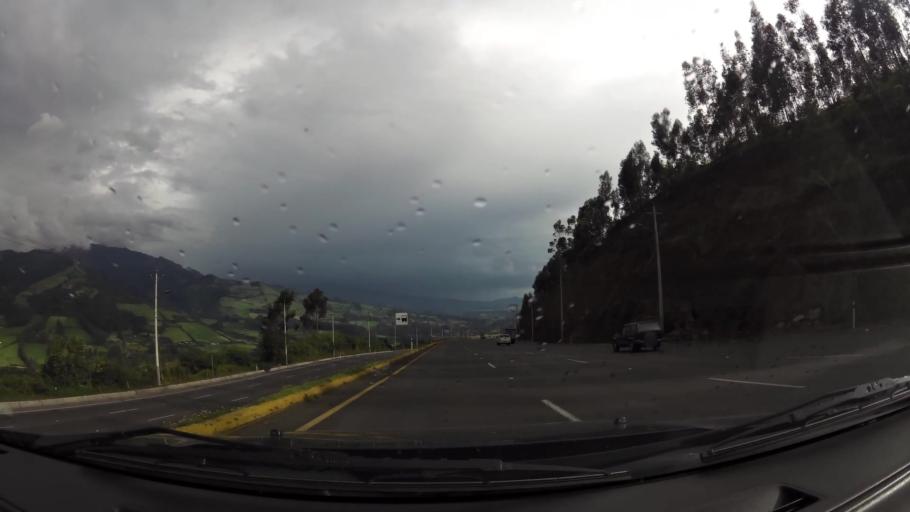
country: EC
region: Pichincha
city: Sangolqui
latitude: -0.3907
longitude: -78.5352
